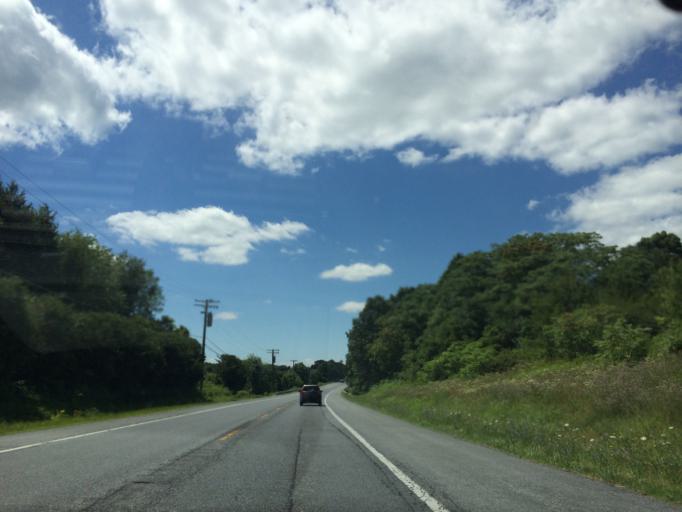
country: US
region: Maryland
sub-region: Carroll County
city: New Windsor
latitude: 39.4540
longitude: -77.0768
